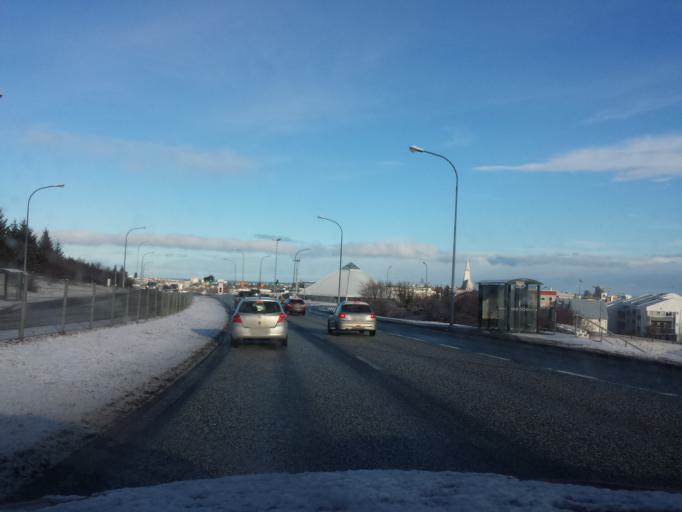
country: IS
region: Capital Region
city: Kopavogur
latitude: 64.1300
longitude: -21.9136
